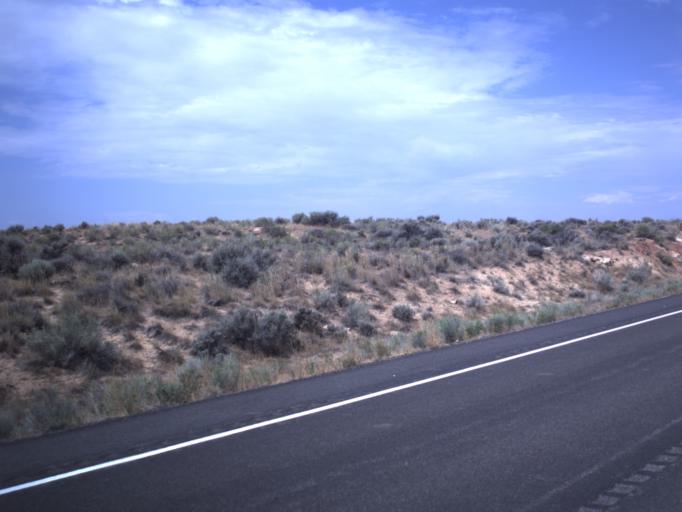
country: US
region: Utah
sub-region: Uintah County
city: Naples
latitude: 40.2522
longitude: -109.4284
